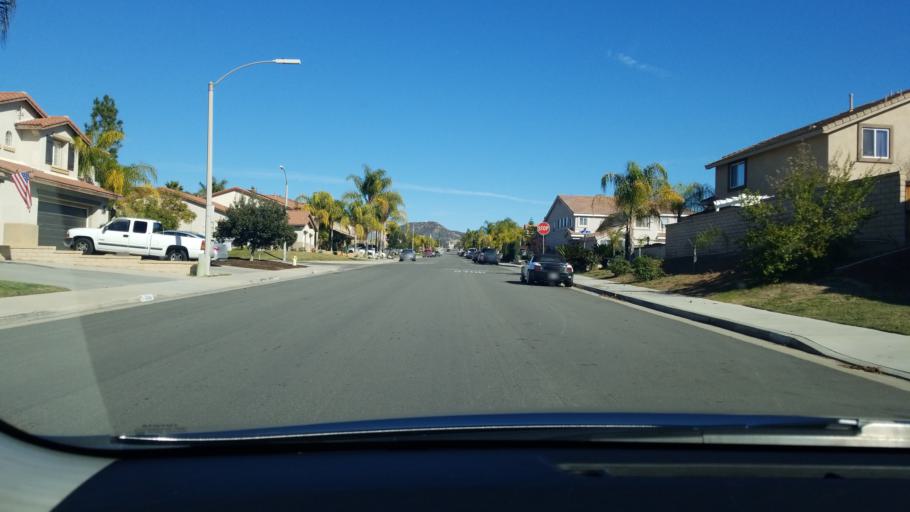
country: US
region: California
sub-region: Riverside County
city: Murrieta
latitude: 33.5848
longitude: -117.2262
